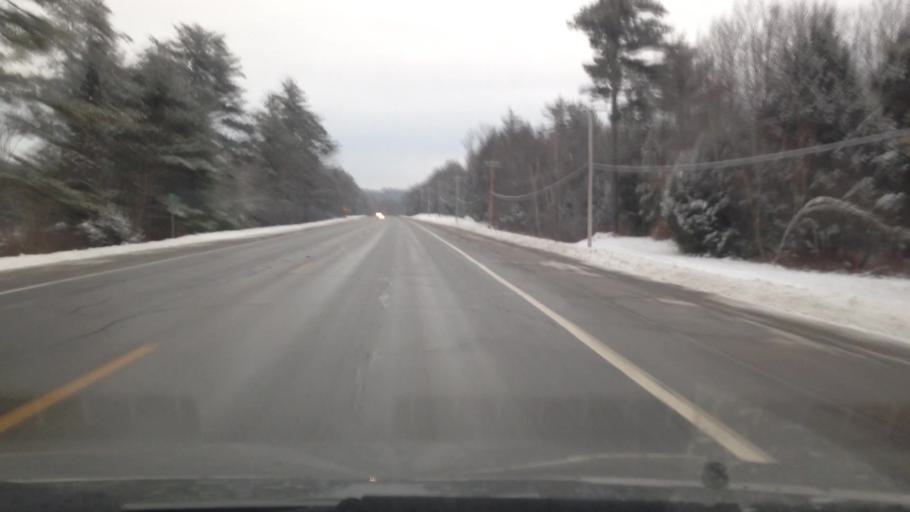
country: US
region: New Hampshire
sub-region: Cheshire County
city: Keene
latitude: 42.9872
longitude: -72.2579
